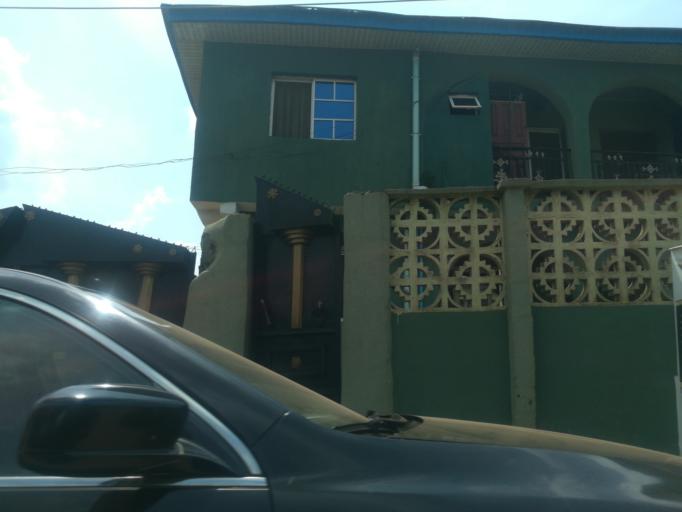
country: NG
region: Oyo
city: Ibadan
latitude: 7.4347
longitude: 3.9426
